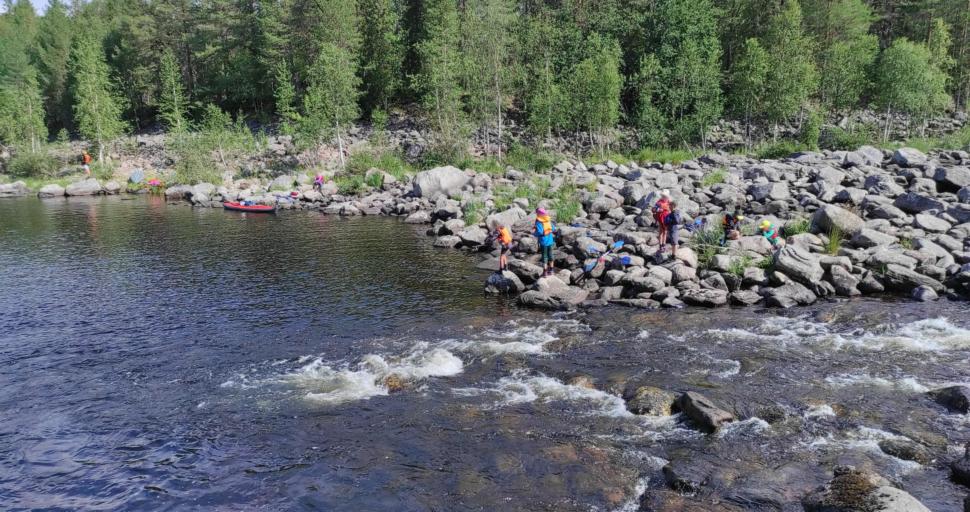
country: RU
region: Murmansk
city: Poyakonda
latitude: 66.6762
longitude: 32.8620
